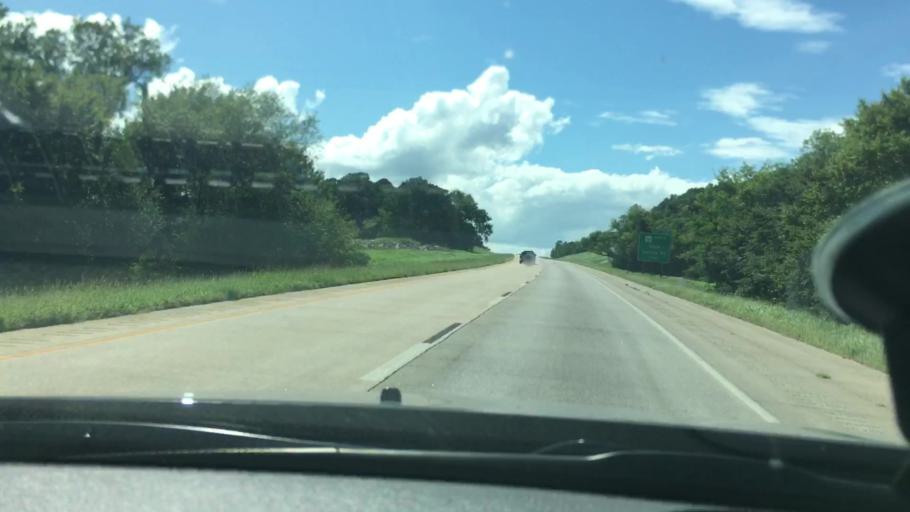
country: US
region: Oklahoma
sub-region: Sequoyah County
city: Vian
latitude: 35.4917
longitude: -95.0562
